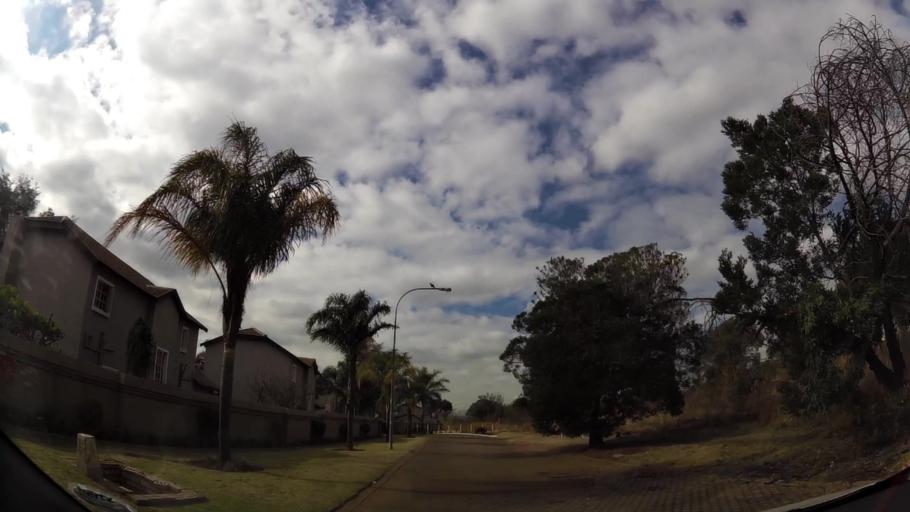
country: ZA
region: Gauteng
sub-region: City of Johannesburg Metropolitan Municipality
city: Roodepoort
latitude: -26.1026
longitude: 27.8779
